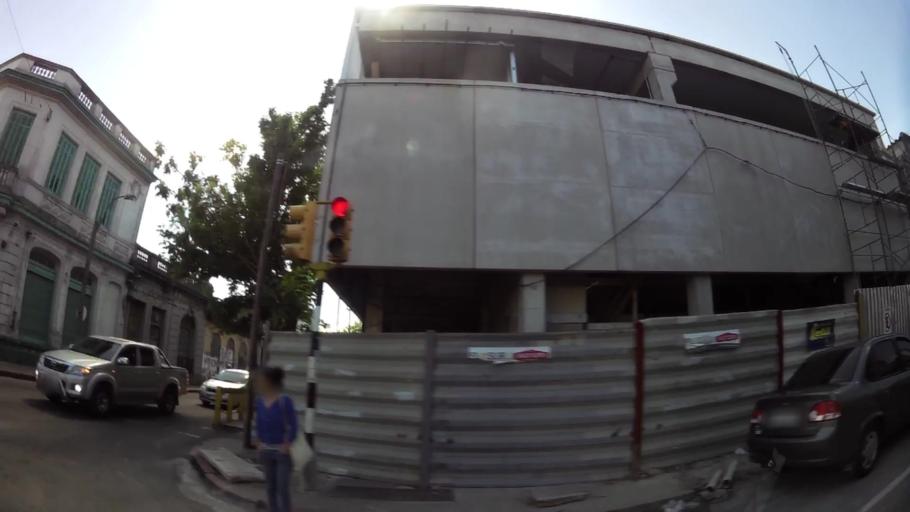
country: UY
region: Montevideo
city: Montevideo
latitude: -34.8992
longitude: -56.1887
